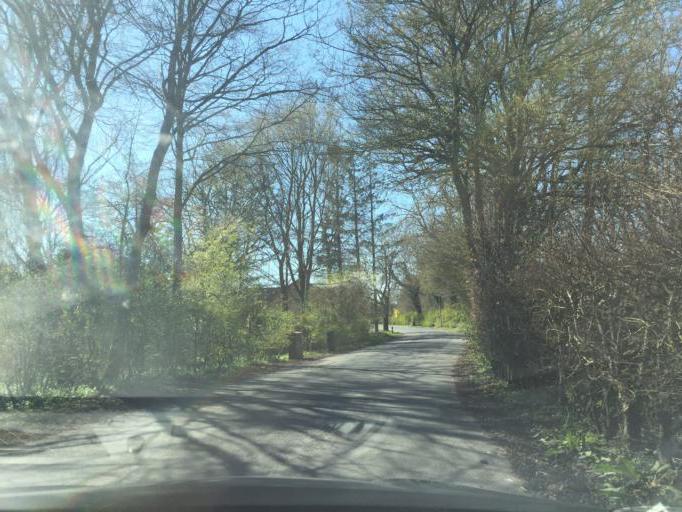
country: DK
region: South Denmark
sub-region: Faaborg-Midtfyn Kommune
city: Arslev
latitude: 55.2874
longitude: 10.5377
